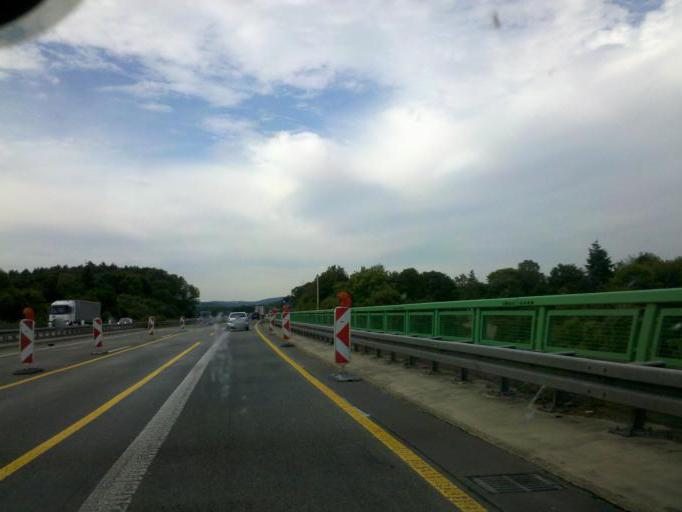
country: DE
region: North Rhine-Westphalia
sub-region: Regierungsbezirk Arnsberg
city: Luedenscheid
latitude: 51.2169
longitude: 7.6687
